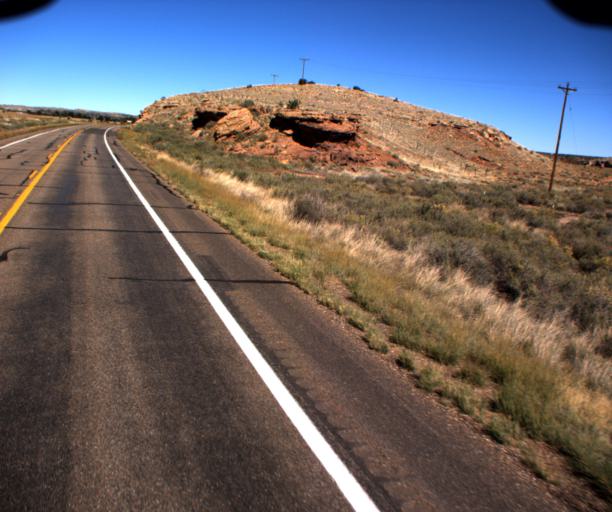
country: US
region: Arizona
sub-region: Apache County
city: Saint Johns
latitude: 34.4198
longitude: -109.4110
